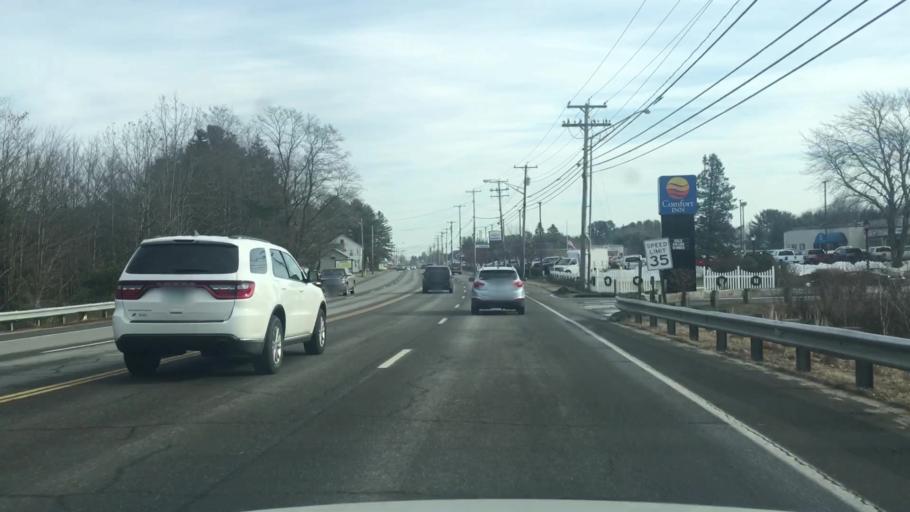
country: US
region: Maine
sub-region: Sagadahoc County
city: Topsham
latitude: 43.9120
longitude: -69.9948
